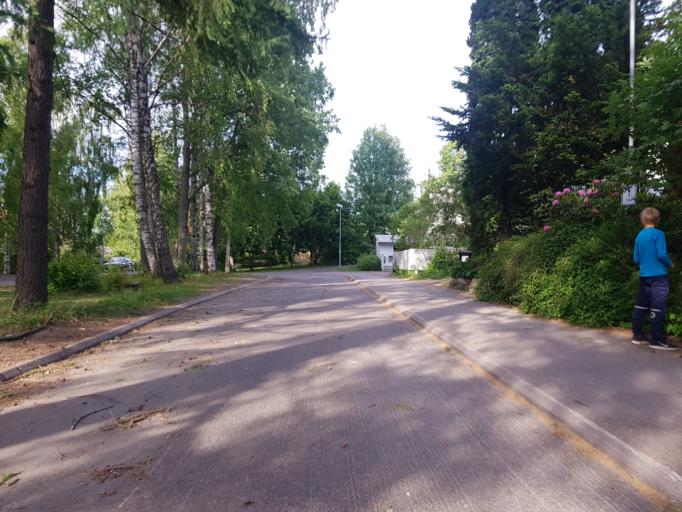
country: FI
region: Uusimaa
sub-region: Helsinki
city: Helsinki
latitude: 60.2246
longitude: 24.9612
